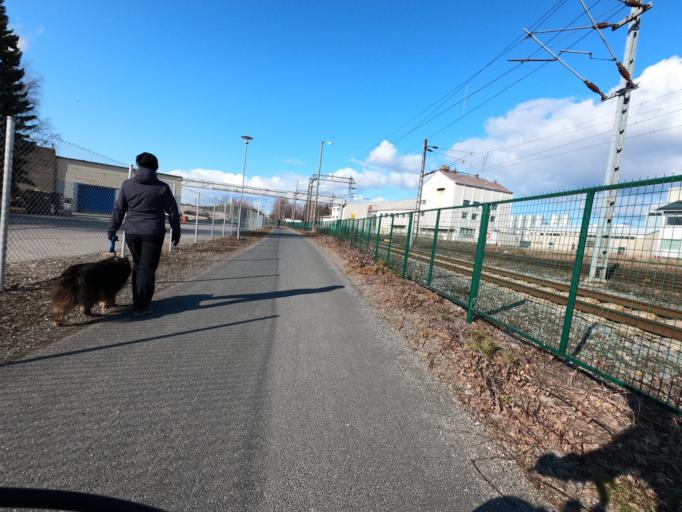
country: FI
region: North Karelia
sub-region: Joensuu
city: Joensuu
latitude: 62.6031
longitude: 29.7799
